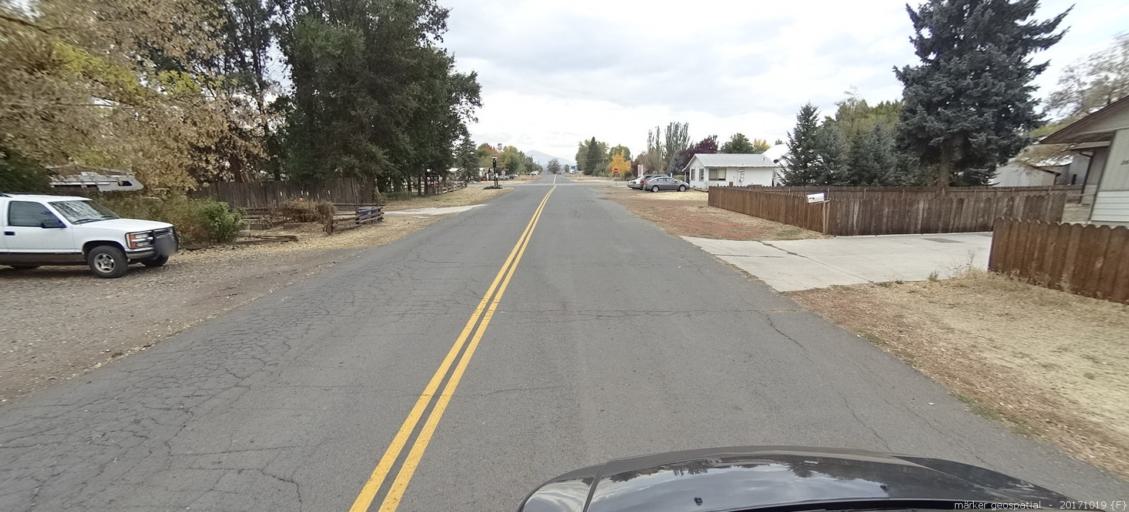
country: US
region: California
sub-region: Shasta County
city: Burney
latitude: 41.0509
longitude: -121.4009
